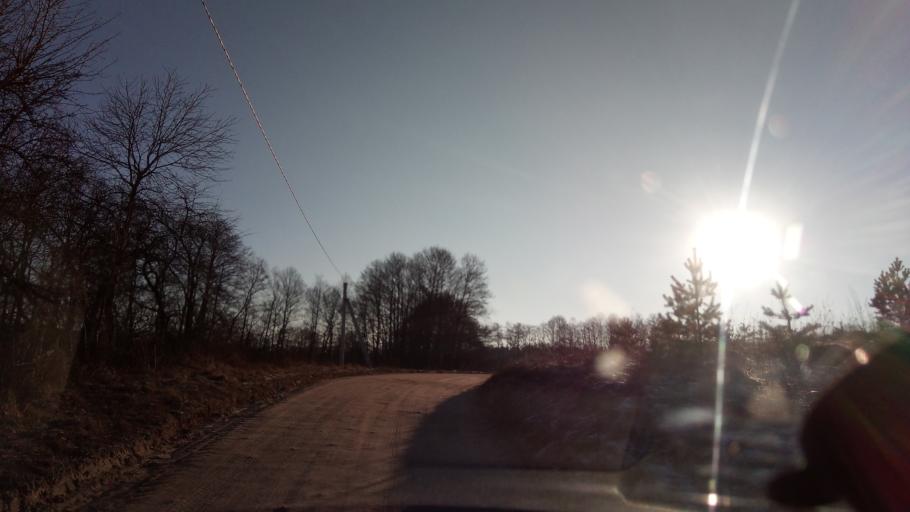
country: LT
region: Alytaus apskritis
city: Druskininkai
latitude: 54.1043
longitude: 24.0150
